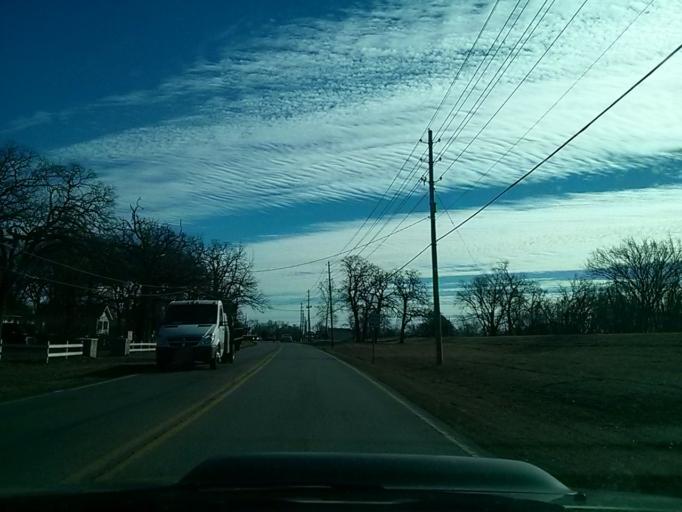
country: US
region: Oklahoma
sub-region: Tulsa County
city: Jenks
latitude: 36.0242
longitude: -95.9873
